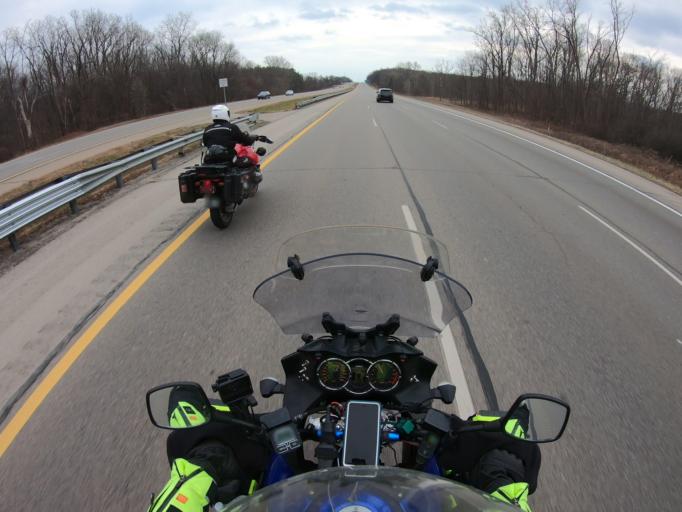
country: US
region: Michigan
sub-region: Oakland County
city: Holly
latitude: 42.8353
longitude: -83.5814
